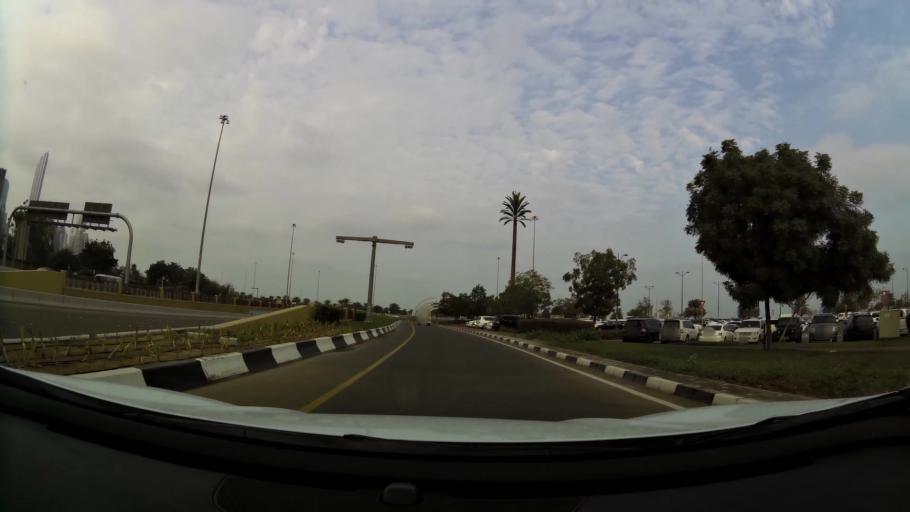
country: AE
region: Abu Dhabi
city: Abu Dhabi
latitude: 24.5001
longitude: 54.3665
